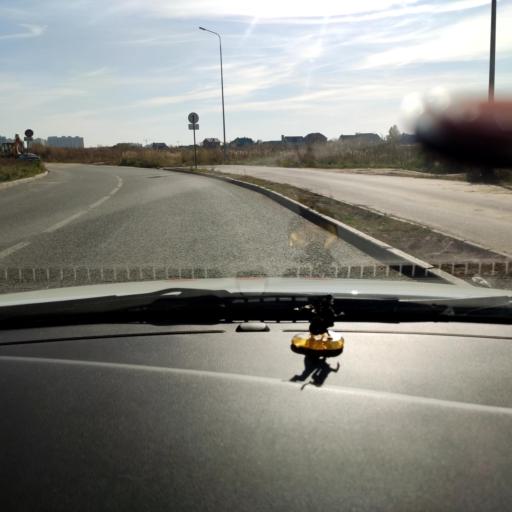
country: RU
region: Tatarstan
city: Osinovo
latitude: 55.8634
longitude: 48.8724
